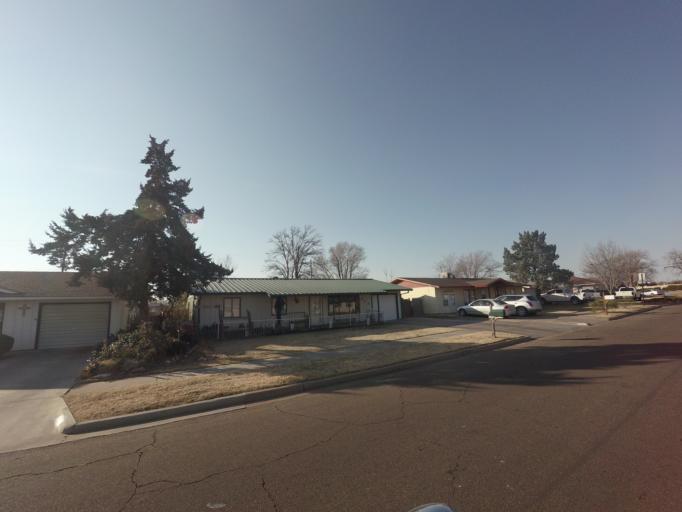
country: US
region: New Mexico
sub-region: Curry County
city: Clovis
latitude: 34.4161
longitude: -103.2132
